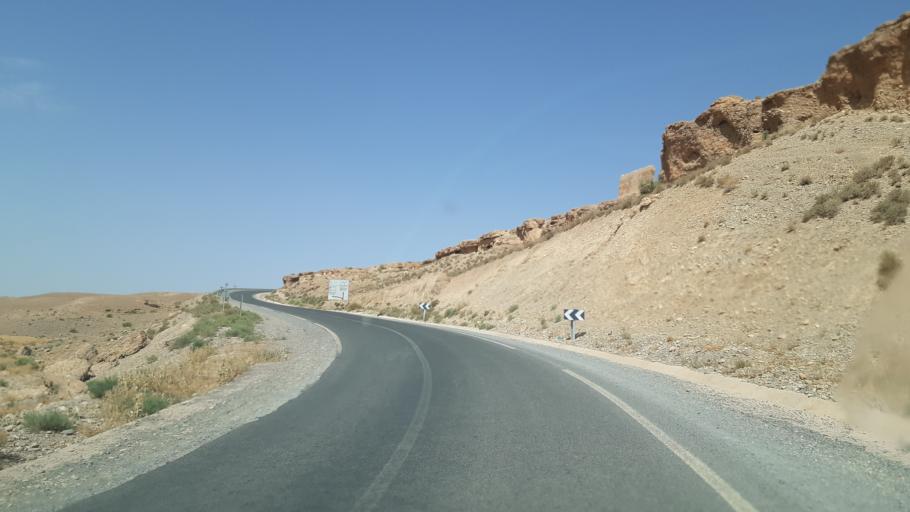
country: MA
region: Meknes-Tafilalet
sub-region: Errachidia
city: Amouguer
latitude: 32.2346
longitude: -4.7315
